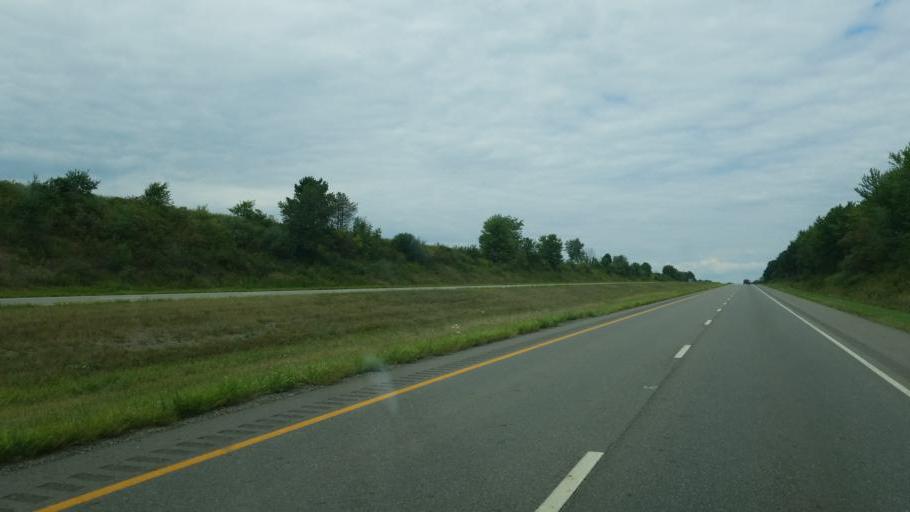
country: US
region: Ohio
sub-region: Columbiana County
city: Columbiana
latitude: 40.9011
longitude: -80.7225
